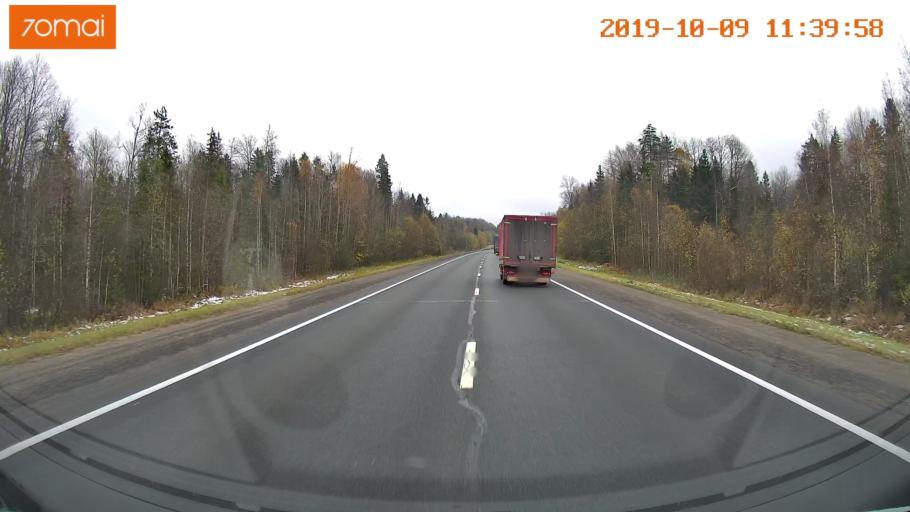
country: RU
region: Vologda
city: Gryazovets
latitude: 58.9495
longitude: 40.1712
